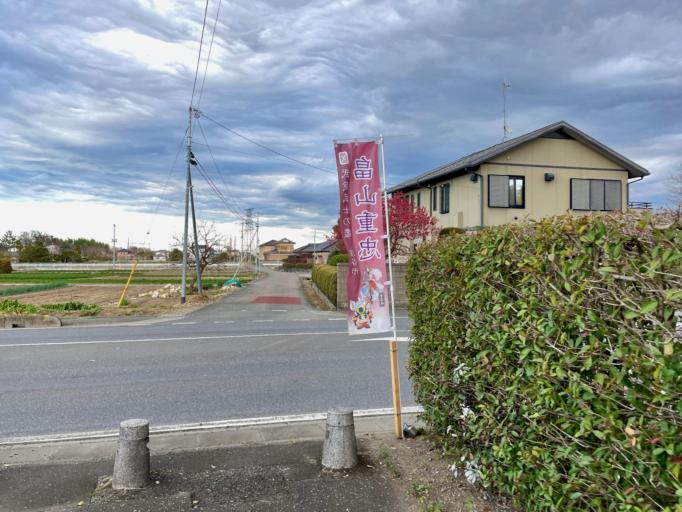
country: JP
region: Saitama
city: Yorii
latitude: 36.1279
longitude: 139.2666
